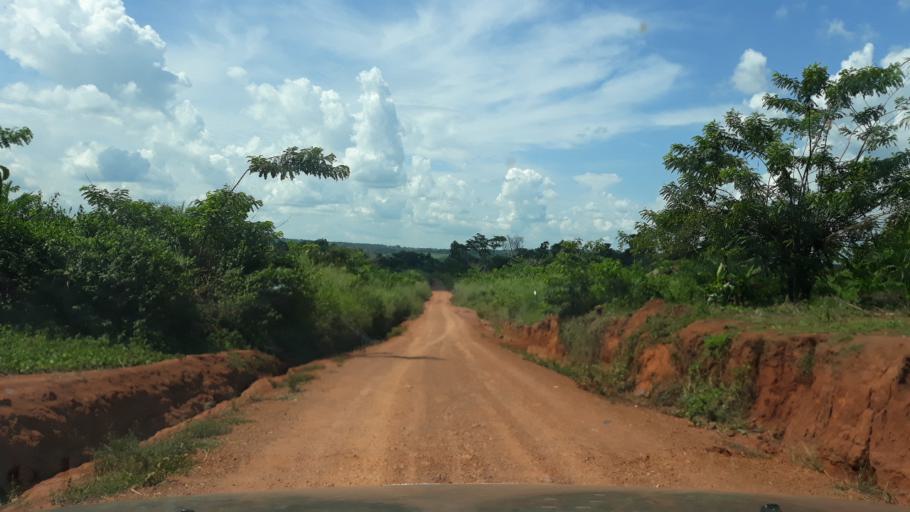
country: CD
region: Equateur
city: Businga
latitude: 3.3960
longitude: 20.3748
